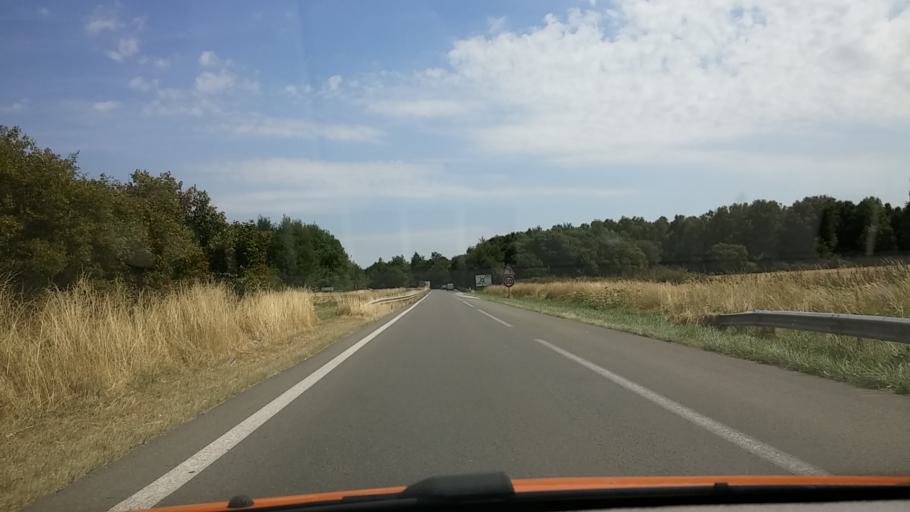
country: FR
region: Ile-de-France
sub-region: Departement de Seine-et-Marne
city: Serris
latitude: 48.8324
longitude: 2.7943
